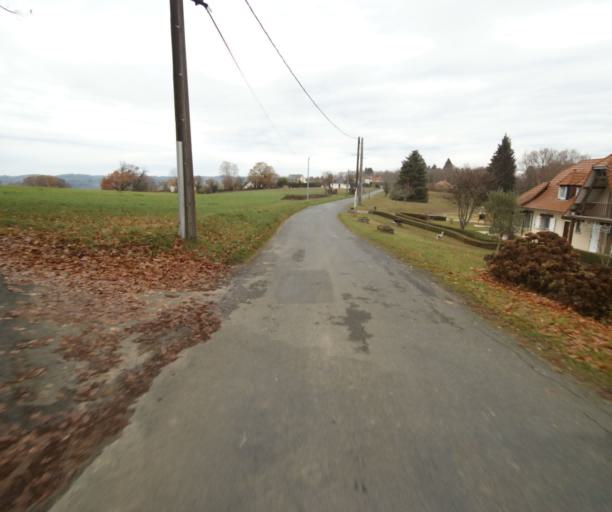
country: FR
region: Limousin
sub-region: Departement de la Correze
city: Sainte-Fortunade
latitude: 45.2285
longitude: 1.7634
